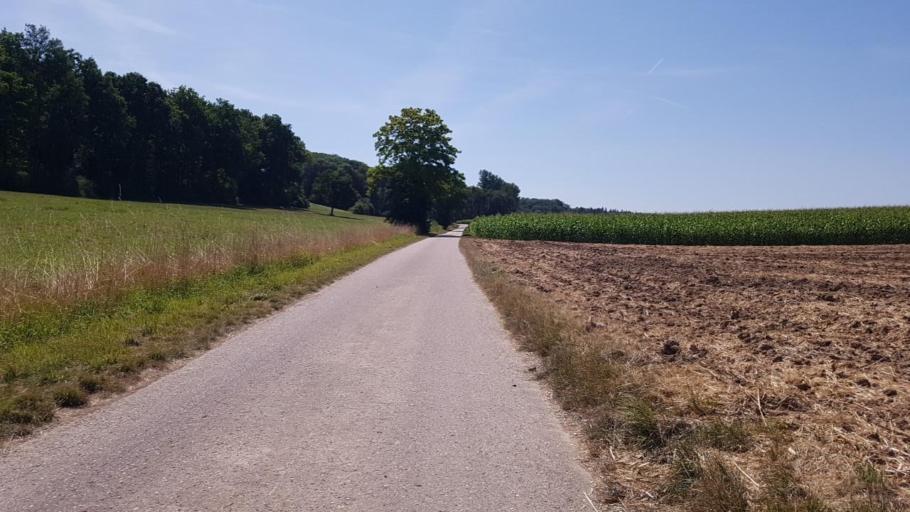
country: DE
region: Baden-Wuerttemberg
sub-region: Karlsruhe Region
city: Sulzfeld
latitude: 49.1616
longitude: 8.8589
